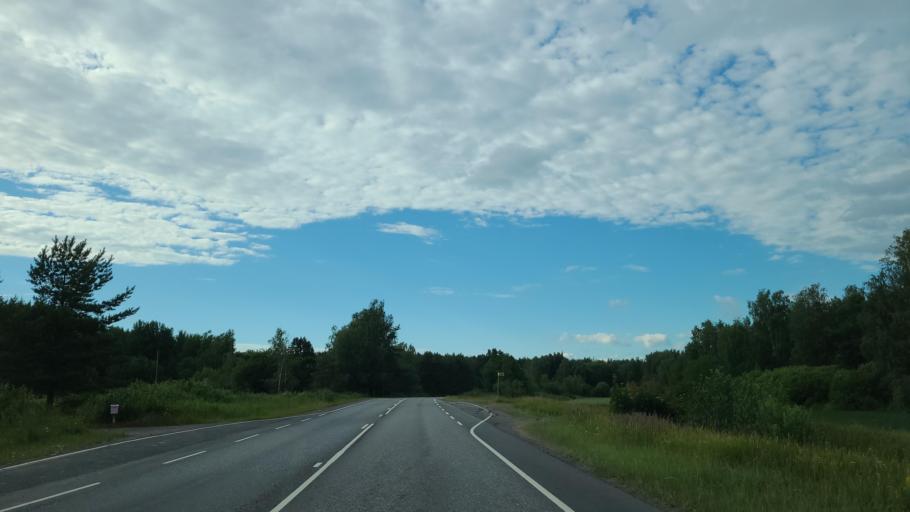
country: FI
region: Varsinais-Suomi
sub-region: Turku
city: Merimasku
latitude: 60.4284
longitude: 21.8959
